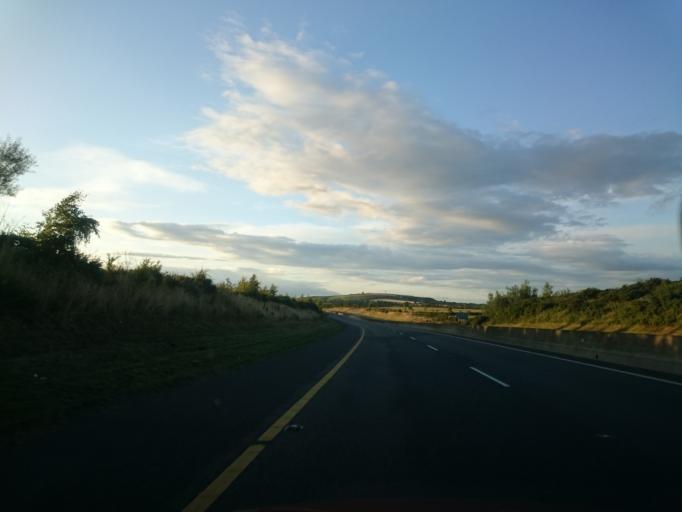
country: IE
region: Leinster
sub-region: Loch Garman
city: Gorey
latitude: 52.6742
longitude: -6.2579
